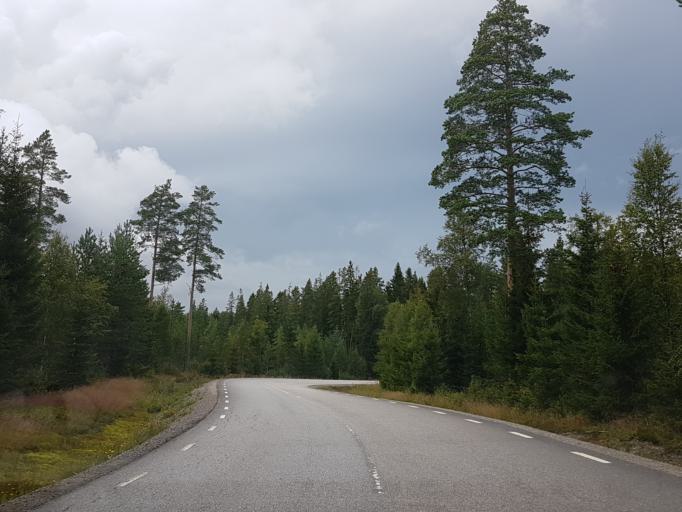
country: SE
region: Vaesterbotten
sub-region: Umea Kommun
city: Holmsund
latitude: 63.7978
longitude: 20.3673
